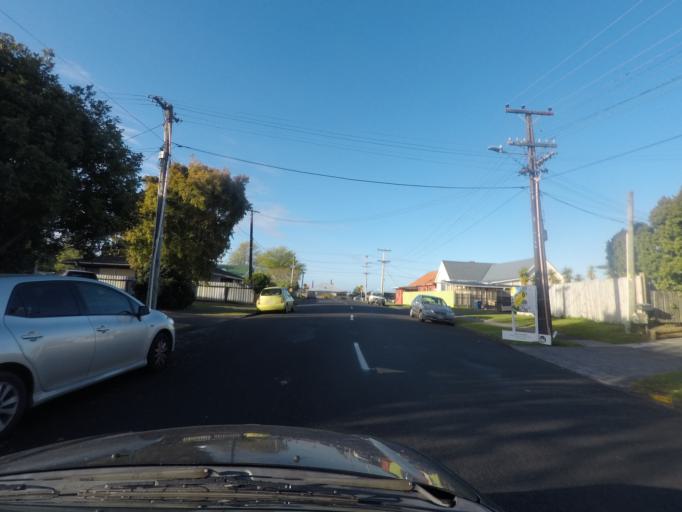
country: NZ
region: Auckland
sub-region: Auckland
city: Waitakere
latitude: -36.9062
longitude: 174.6739
